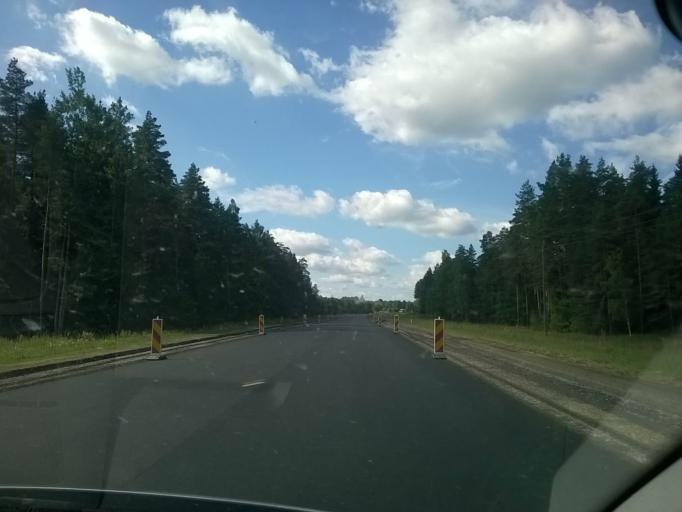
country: EE
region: Vorumaa
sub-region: Voru linn
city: Voru
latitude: 57.7989
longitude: 26.9595
